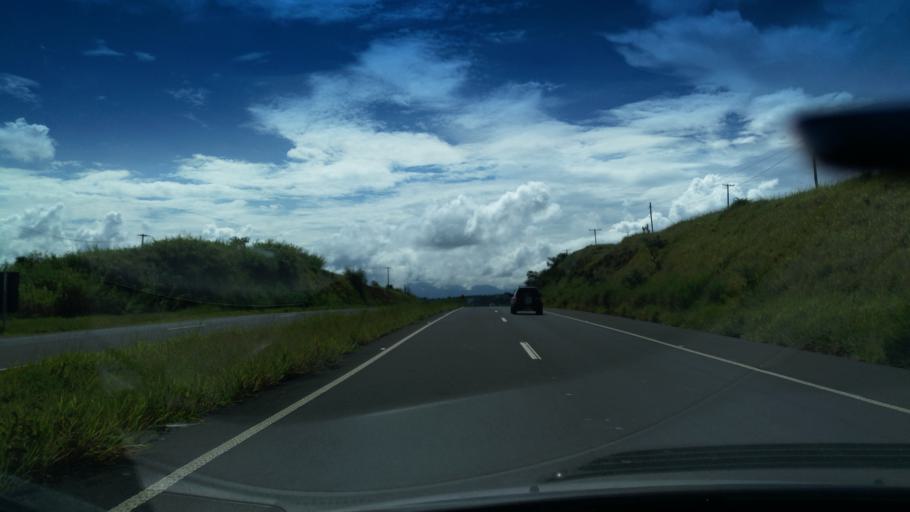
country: BR
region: Sao Paulo
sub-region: Santo Antonio Do Jardim
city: Espirito Santo do Pinhal
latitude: -22.1712
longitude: -46.7437
